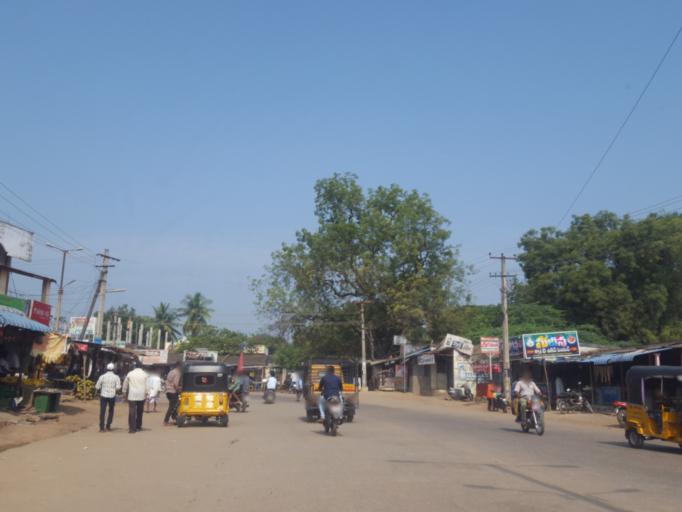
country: IN
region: Telangana
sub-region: Khammam
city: Yellandu
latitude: 17.5951
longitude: 80.3216
